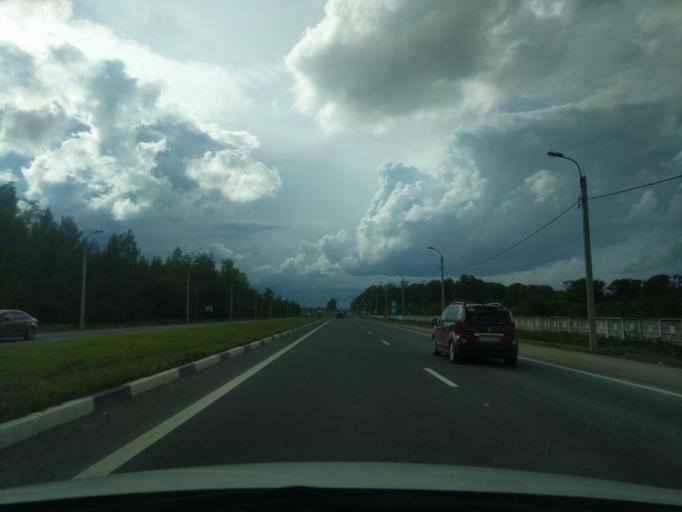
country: RU
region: Jaroslavl
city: Tunoshna
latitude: 57.5407
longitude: 39.9862
